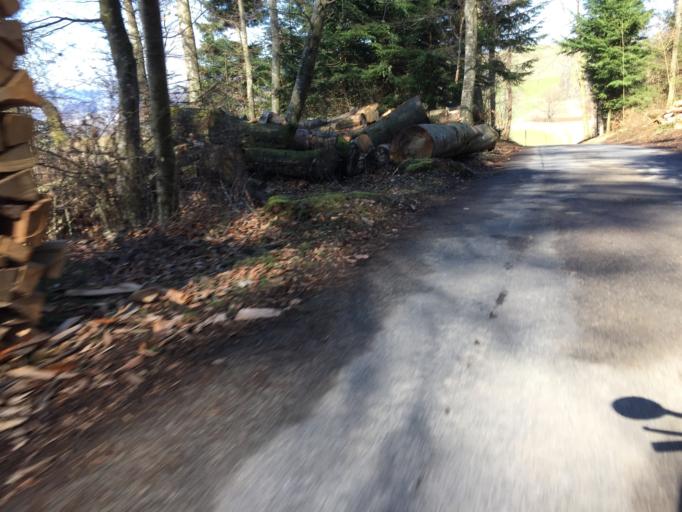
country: CH
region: Bern
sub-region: Bern-Mittelland District
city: Taegertschi
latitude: 46.8981
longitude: 7.5875
